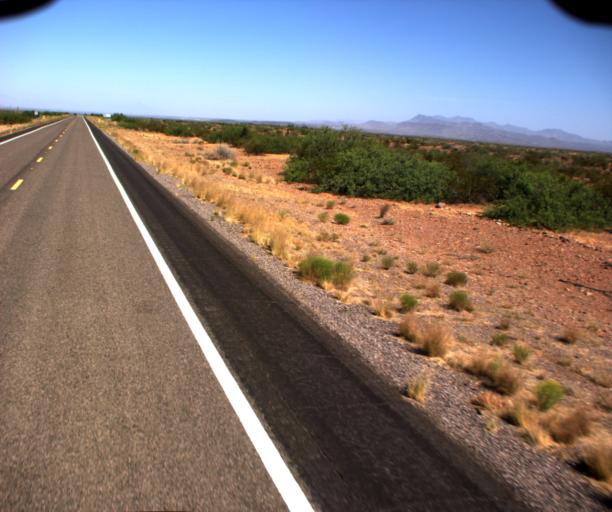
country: US
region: Arizona
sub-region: Graham County
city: Swift Trail Junction
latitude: 32.7619
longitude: -109.4442
